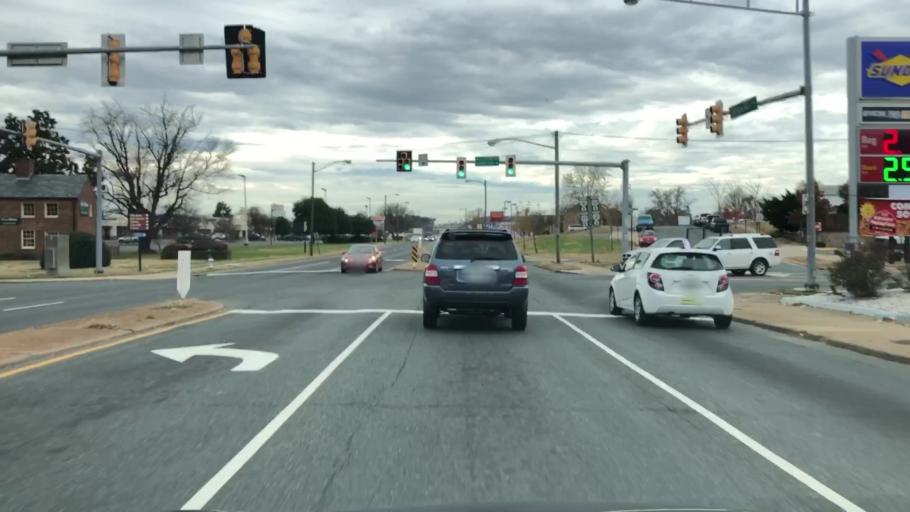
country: US
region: Virginia
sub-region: Stafford County
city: Falmouth
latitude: 38.3184
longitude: -77.4721
